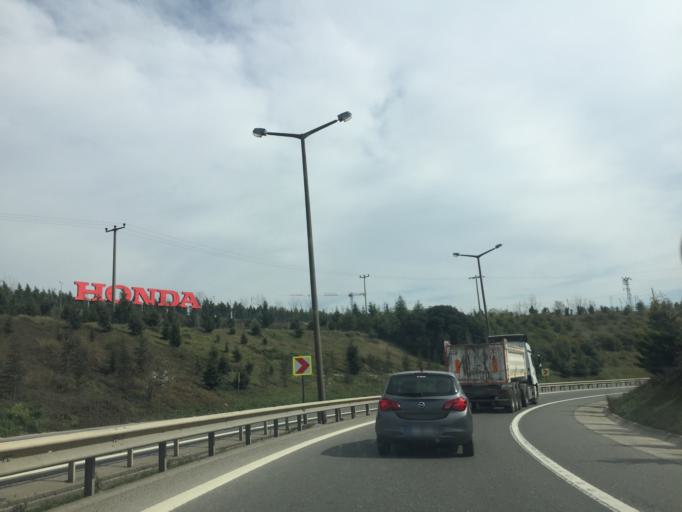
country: TR
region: Kocaeli
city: Balcik
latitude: 40.8711
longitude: 29.3979
